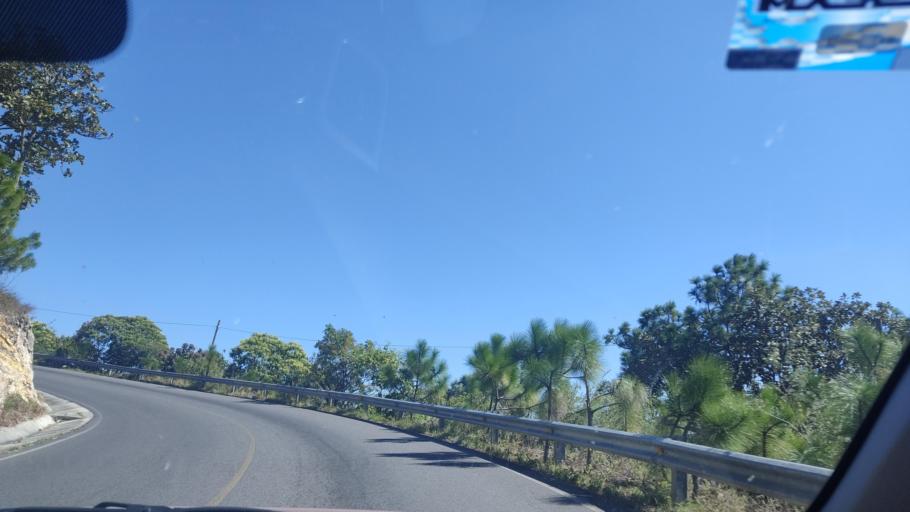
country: MX
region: Nayarit
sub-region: Jala
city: Rosa Blanca
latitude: 21.0981
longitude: -104.3635
